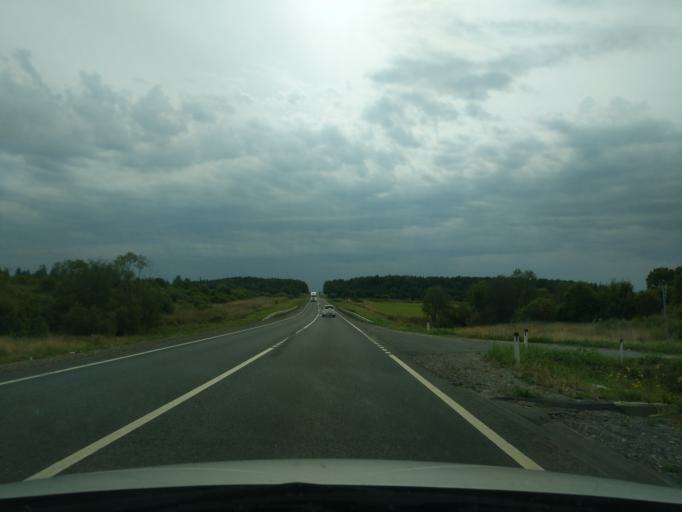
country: RU
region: Kostroma
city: Manturovo
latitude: 58.3109
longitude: 44.7221
